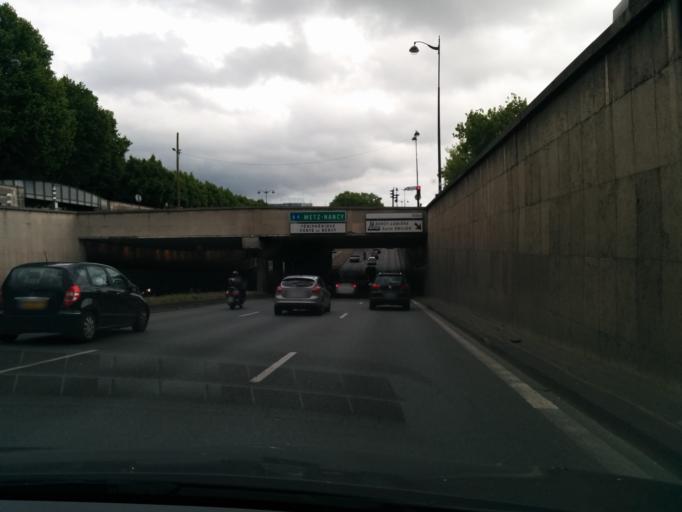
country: FR
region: Ile-de-France
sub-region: Departement du Val-de-Marne
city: Ivry-sur-Seine
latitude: 48.8340
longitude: 2.3816
